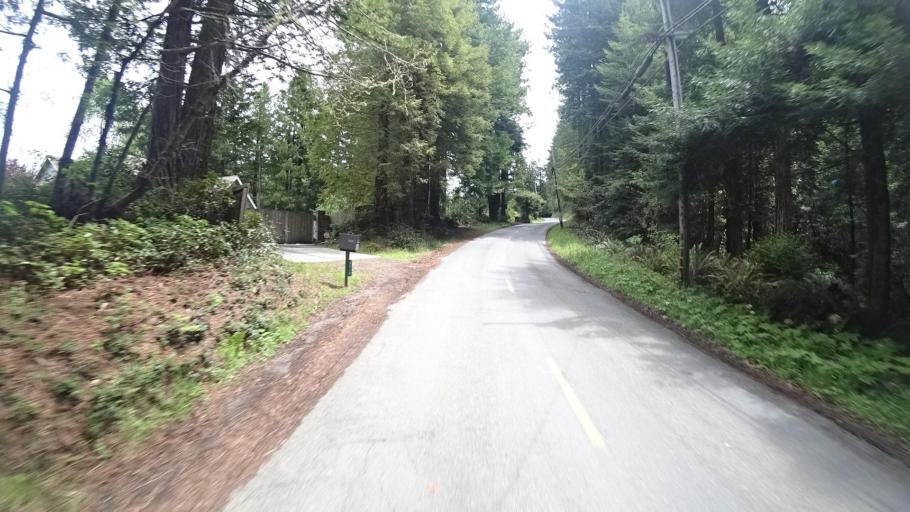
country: US
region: California
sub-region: Humboldt County
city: Bayside
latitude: 40.8007
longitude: -124.0403
